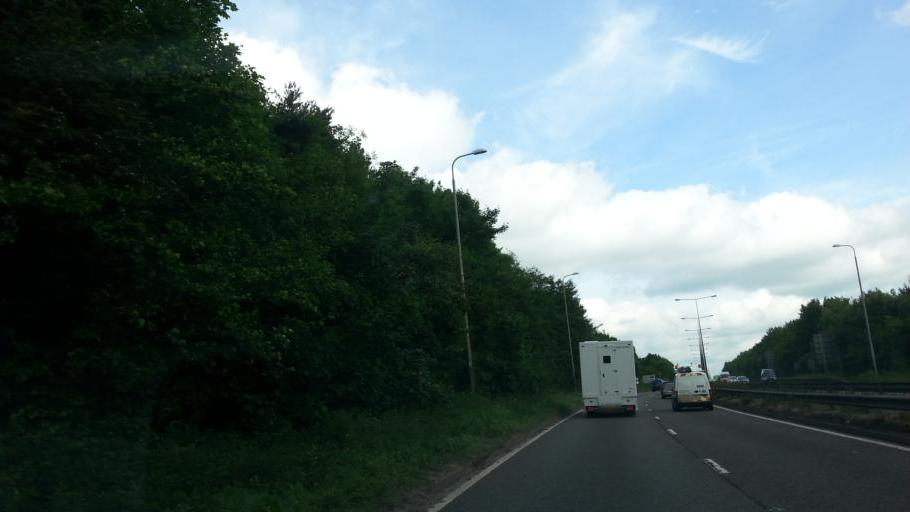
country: GB
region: England
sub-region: Staffordshire
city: Newcastle under Lyme
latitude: 53.0434
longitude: -2.2215
